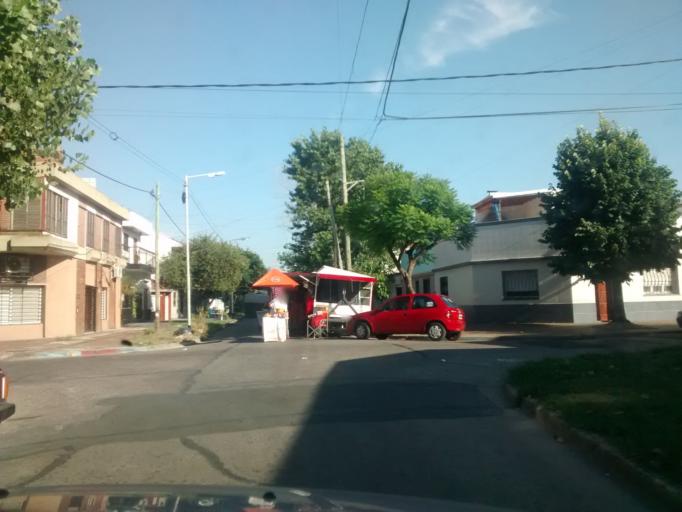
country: AR
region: Buenos Aires
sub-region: Partido de Avellaneda
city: Avellaneda
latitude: -34.6831
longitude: -58.3520
